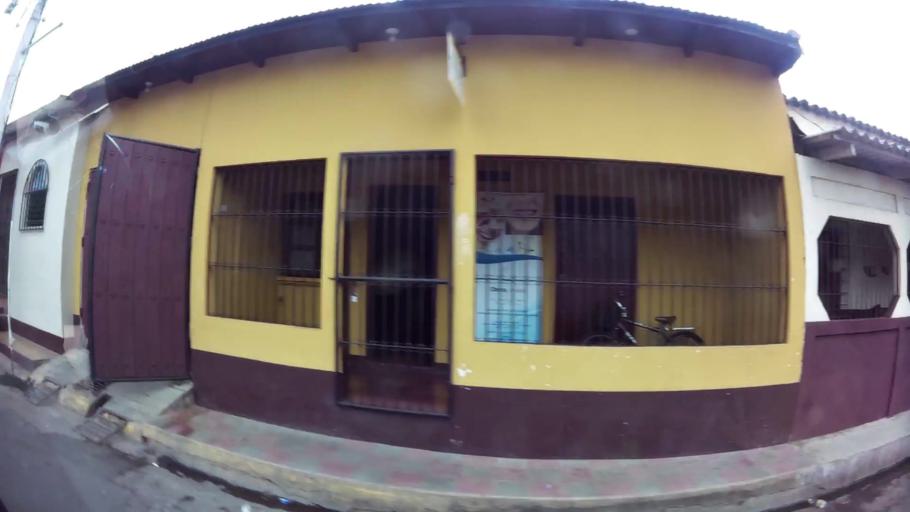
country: NI
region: Leon
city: Leon
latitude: 12.4414
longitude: -86.8708
